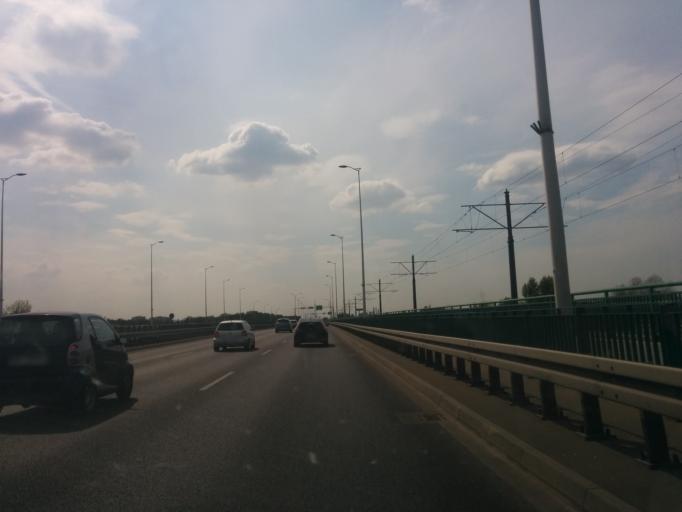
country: PL
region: Masovian Voivodeship
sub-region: Warszawa
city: Bielany
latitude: 52.3064
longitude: 20.9506
